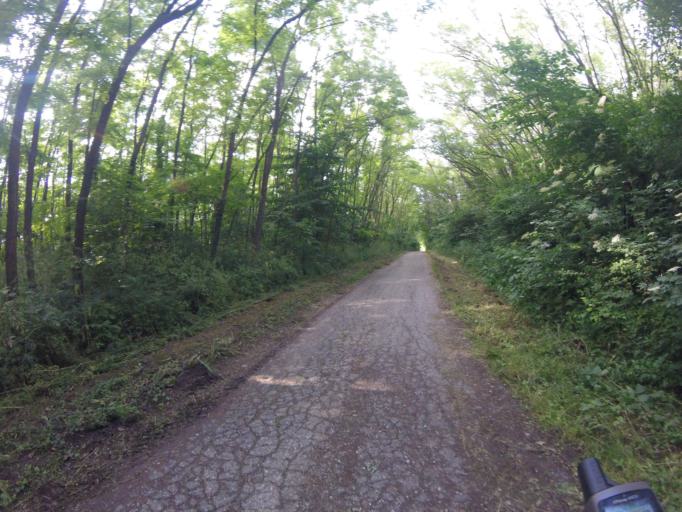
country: HU
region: Zala
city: Zalaszentgrot
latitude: 46.8822
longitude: 17.1263
